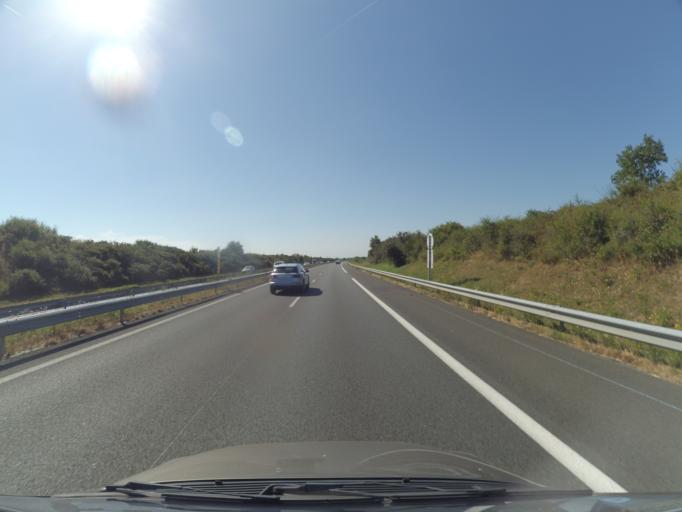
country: FR
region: Pays de la Loire
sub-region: Departement de la Vendee
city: Bournezeau
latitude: 46.6146
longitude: -1.1409
